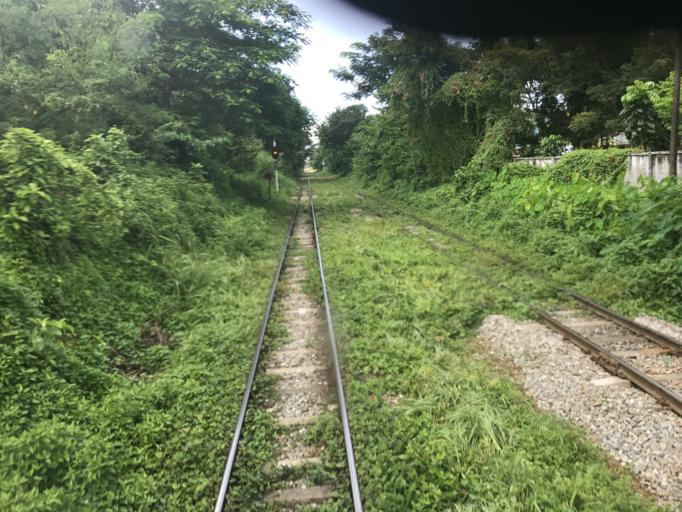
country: MM
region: Yangon
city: Yangon
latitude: 16.8952
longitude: 96.1011
